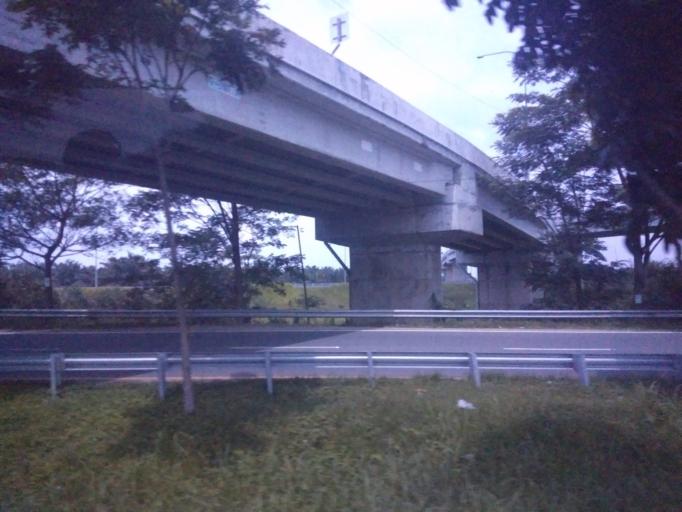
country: ID
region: North Sumatra
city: Percut
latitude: 3.5994
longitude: 98.8429
